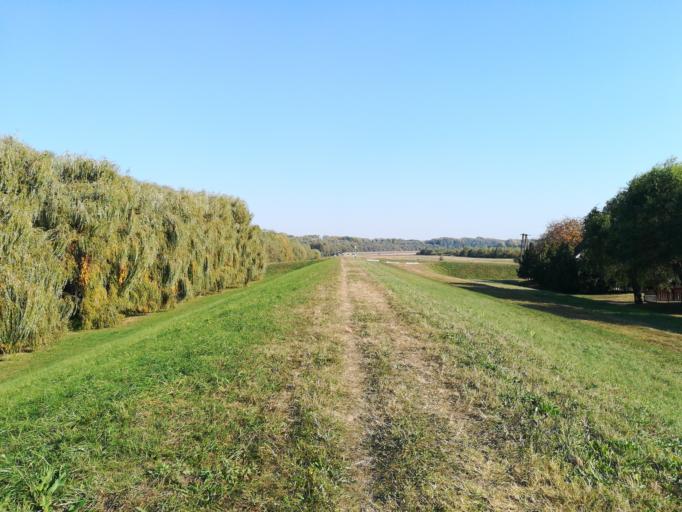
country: HU
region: Bacs-Kiskun
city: Tiszakecske
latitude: 46.9393
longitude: 20.1283
